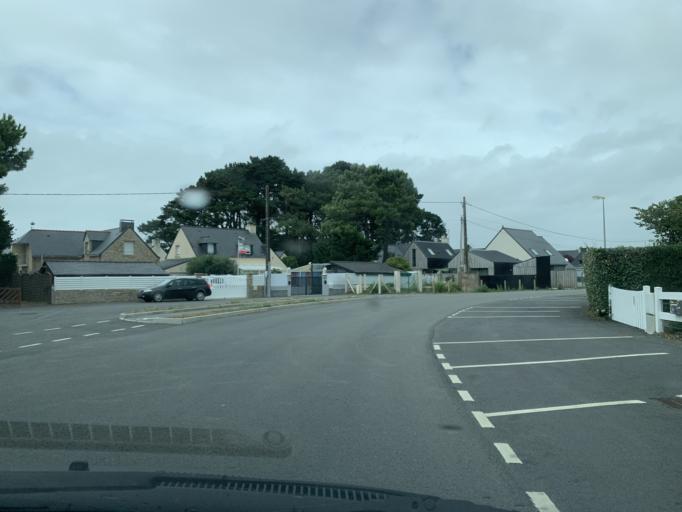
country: FR
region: Brittany
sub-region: Departement du Morbihan
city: Penestin
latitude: 47.4781
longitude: -2.4894
